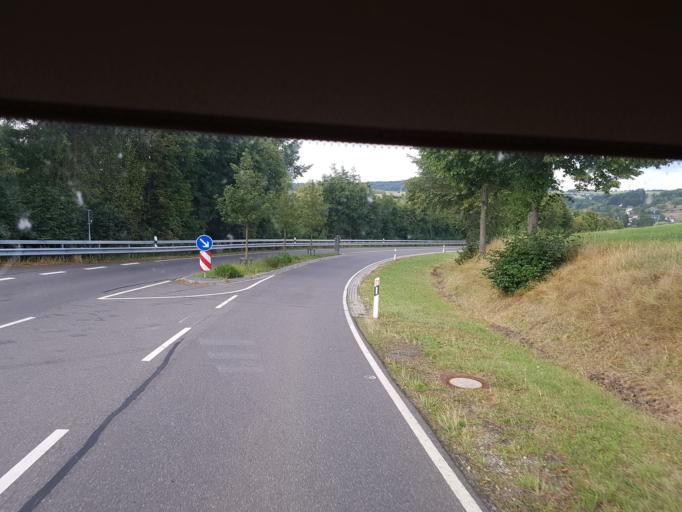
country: DE
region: Rheinland-Pfalz
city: Dockweiler
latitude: 50.2554
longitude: 6.7821
